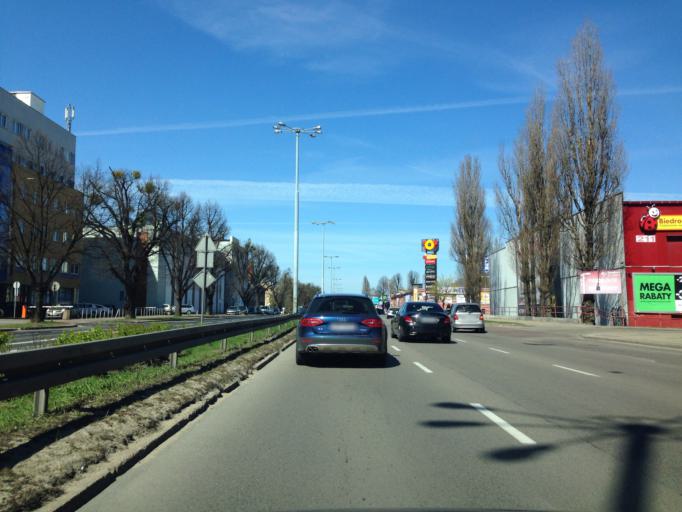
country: PL
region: Pomeranian Voivodeship
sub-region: Sopot
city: Sopot
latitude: 54.3877
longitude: 18.5906
